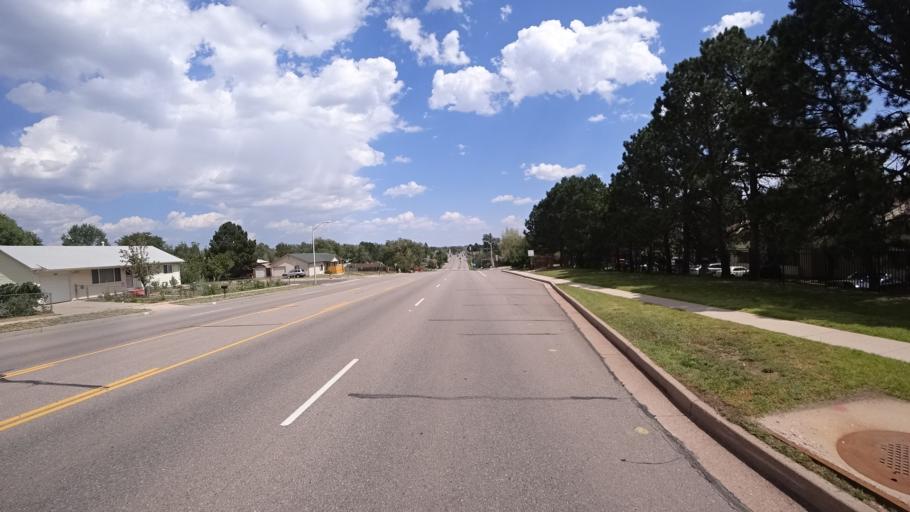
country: US
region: Colorado
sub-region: El Paso County
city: Colorado Springs
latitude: 38.8326
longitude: -104.7818
